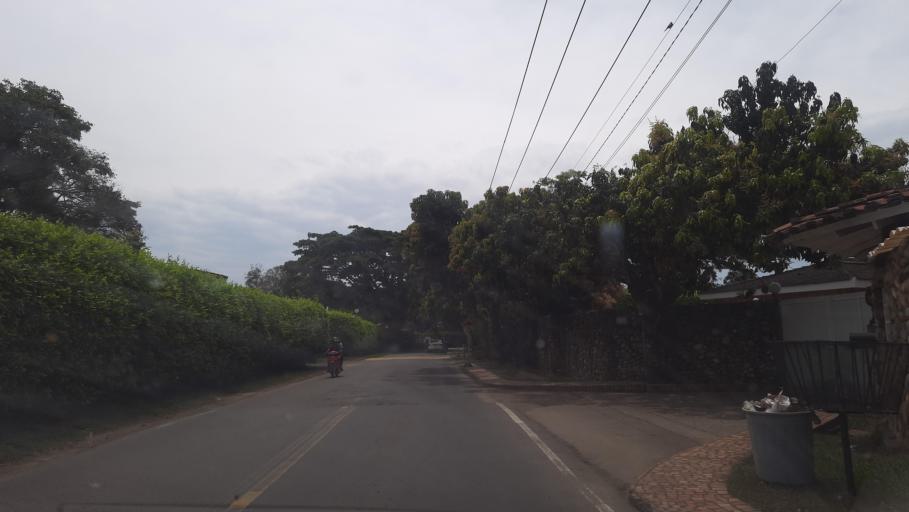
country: CO
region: Valle del Cauca
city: Jamundi
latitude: 3.2697
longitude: -76.5276
